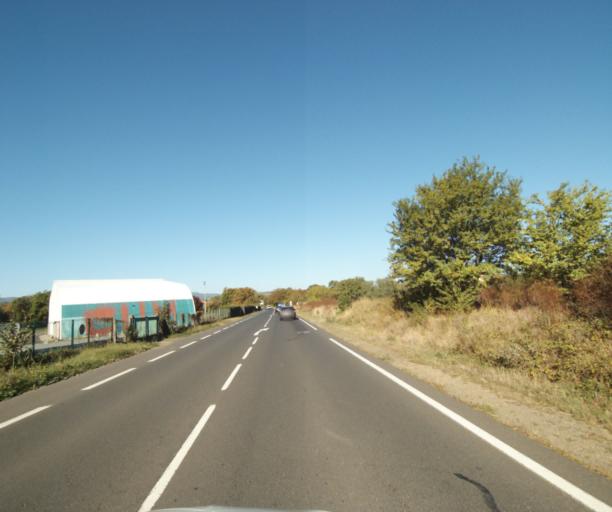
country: FR
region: Auvergne
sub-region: Departement du Puy-de-Dome
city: Gerzat
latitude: 45.8250
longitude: 3.1314
